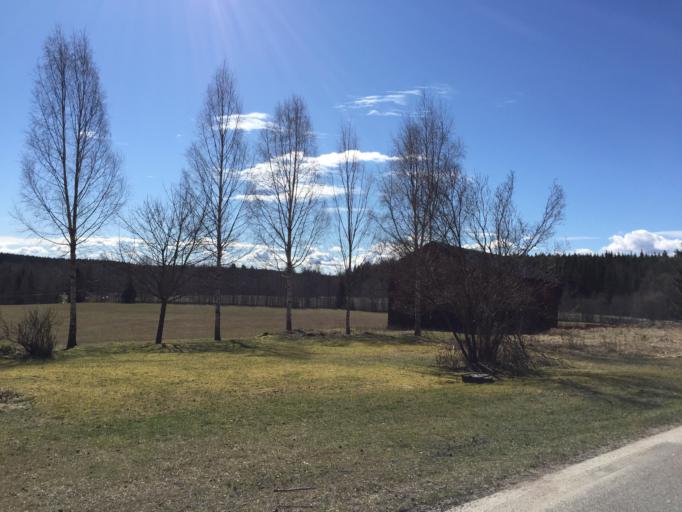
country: SE
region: Soedermanland
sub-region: Vingakers Kommun
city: Vingaker
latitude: 58.9660
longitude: 15.6725
